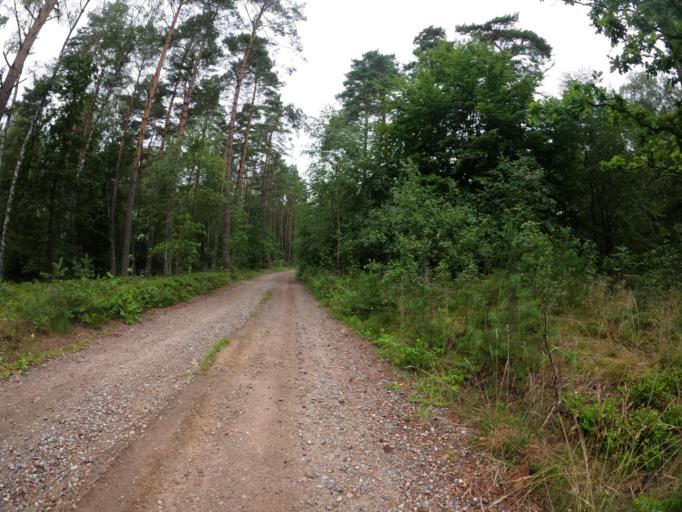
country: PL
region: West Pomeranian Voivodeship
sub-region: Powiat szczecinecki
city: Grzmiaca
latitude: 53.7455
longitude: 16.4990
